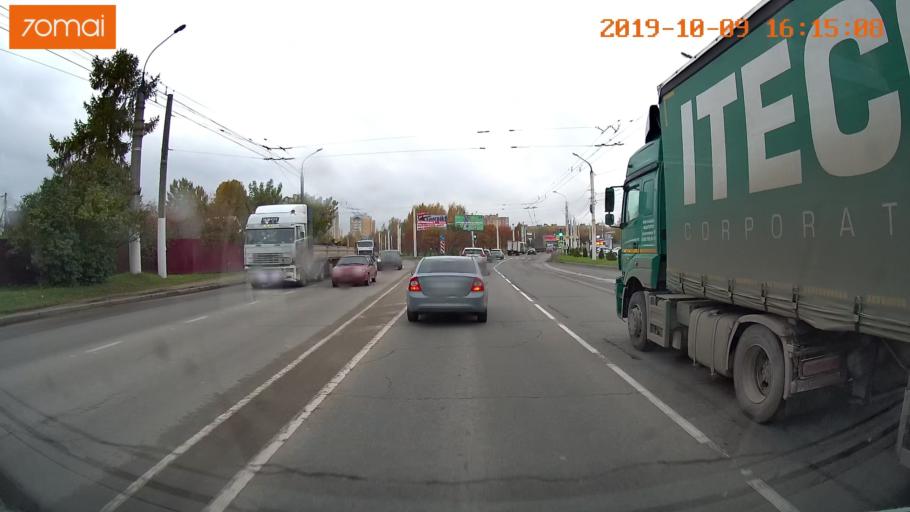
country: RU
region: Kostroma
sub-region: Kostromskoy Rayon
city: Kostroma
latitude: 57.7413
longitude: 40.9188
